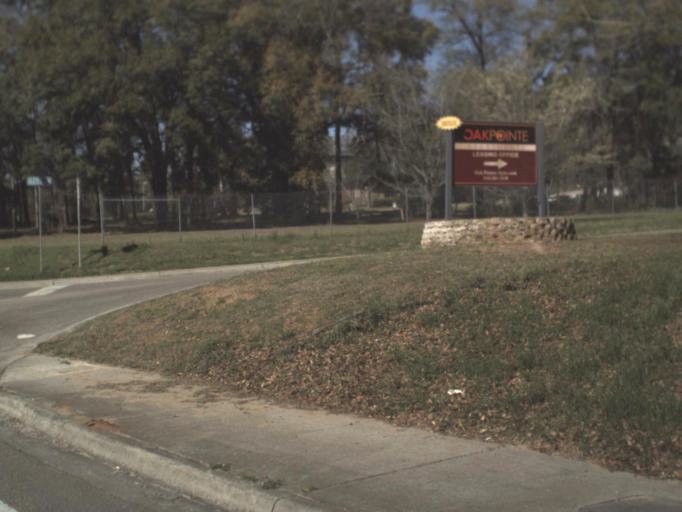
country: US
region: Florida
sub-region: Leon County
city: Tallahassee
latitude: 30.4661
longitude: -84.2297
